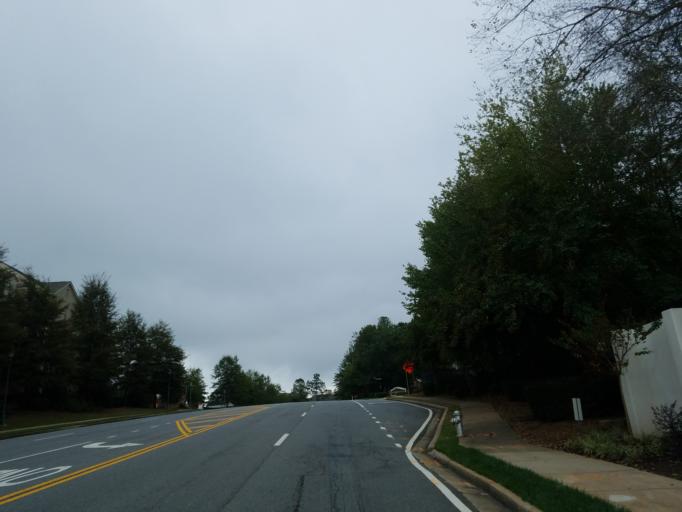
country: US
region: Georgia
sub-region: Fulton County
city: Sandy Springs
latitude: 33.9313
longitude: -84.3611
